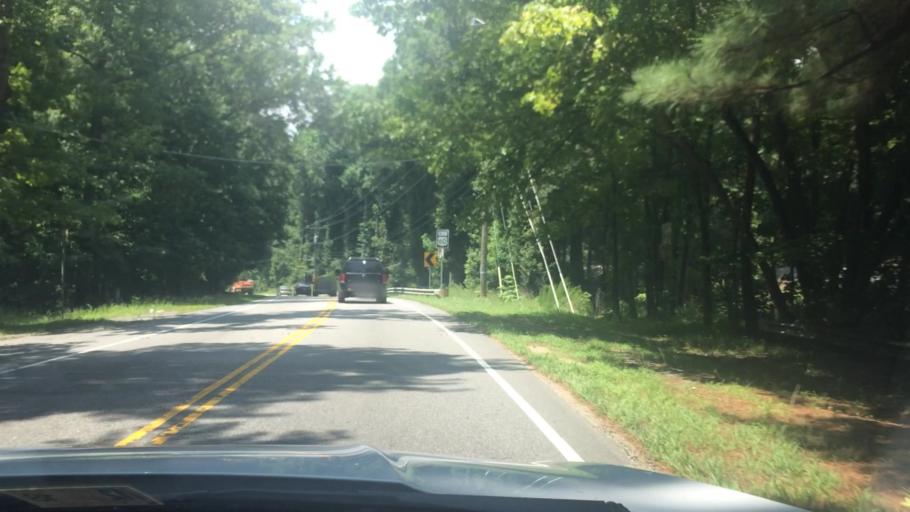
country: US
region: Virginia
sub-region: York County
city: Yorktown
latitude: 37.2089
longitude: -76.5881
